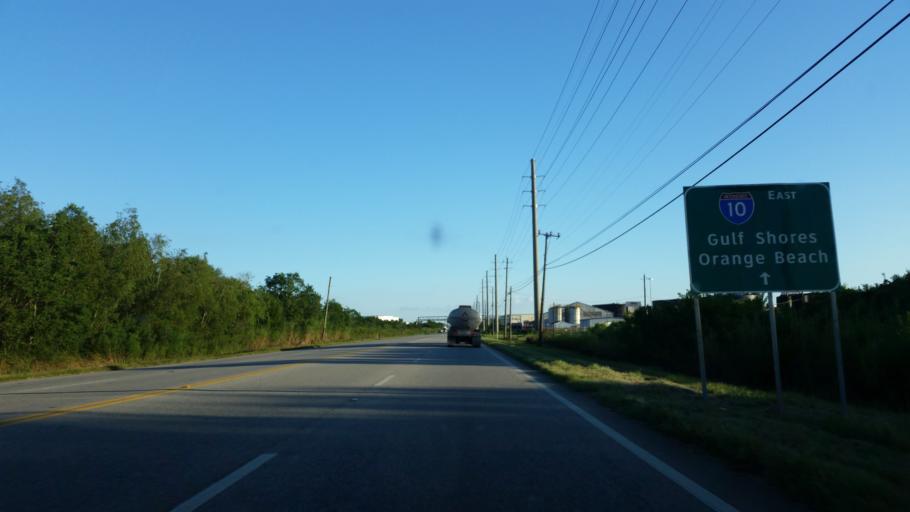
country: US
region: Alabama
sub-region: Mobile County
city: Mobile
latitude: 30.7116
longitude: -88.0335
